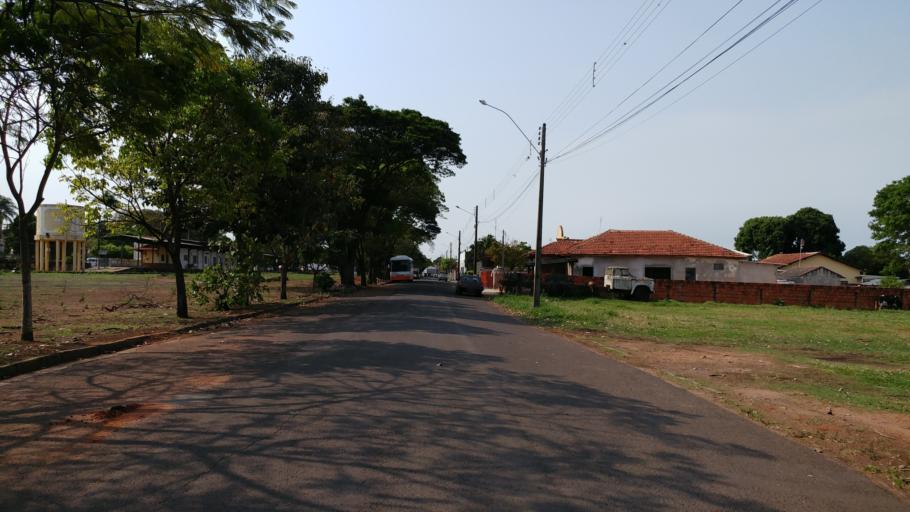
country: BR
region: Sao Paulo
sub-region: Paraguacu Paulista
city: Paraguacu Paulista
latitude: -22.4159
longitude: -50.5726
